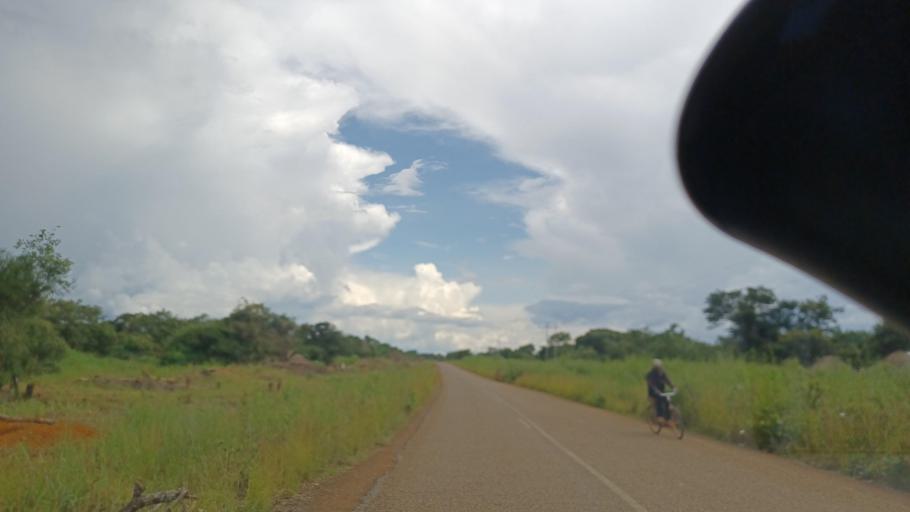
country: ZM
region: North-Western
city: Kasempa
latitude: -13.1239
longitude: 25.8712
